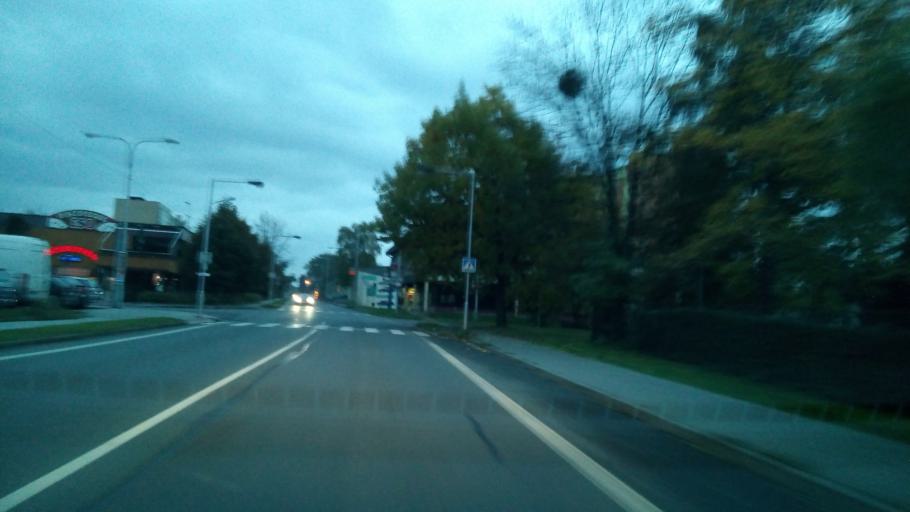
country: CZ
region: Moravskoslezsky
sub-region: Okres Frydek-Mistek
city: Stare Mesto
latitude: 49.6774
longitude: 18.3615
